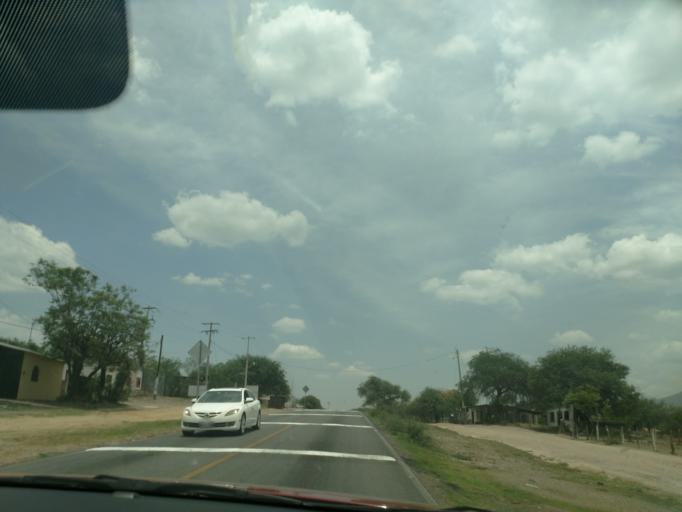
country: MX
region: San Luis Potosi
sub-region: Rioverde
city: Progreso
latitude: 22.0186
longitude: -100.3728
